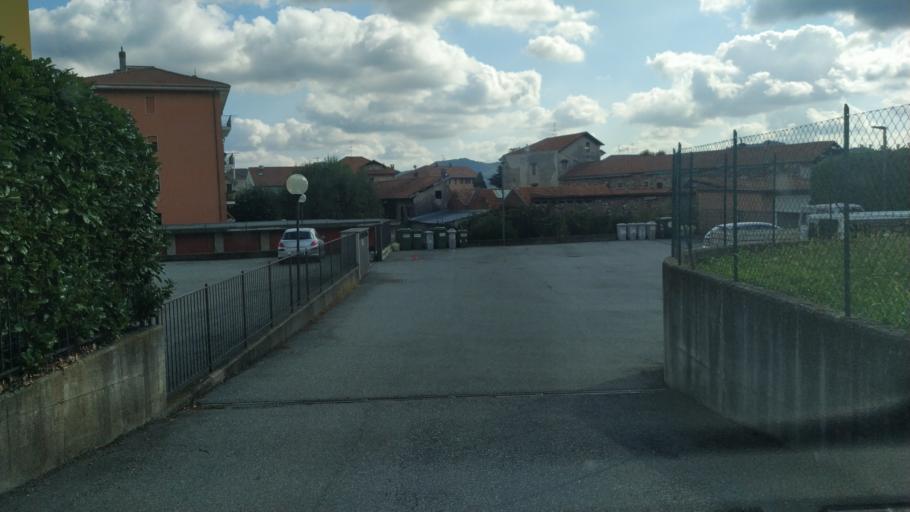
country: IT
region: Piedmont
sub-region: Provincia di Novara
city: Grignasco
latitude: 45.6854
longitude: 8.3335
